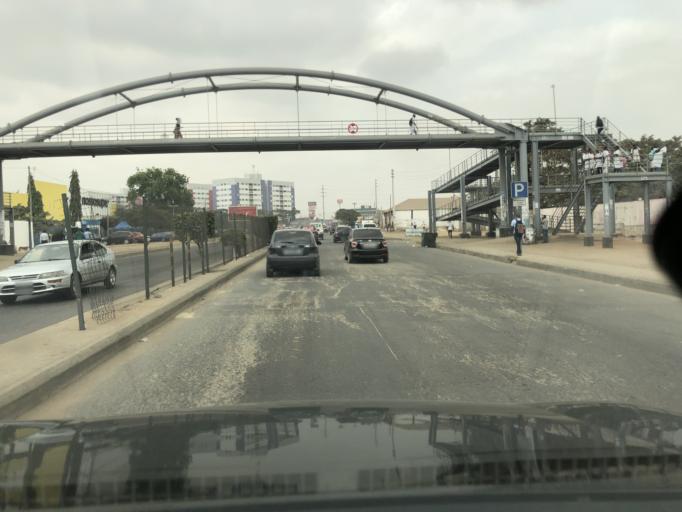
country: AO
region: Luanda
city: Luanda
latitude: -8.8450
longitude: 13.2845
